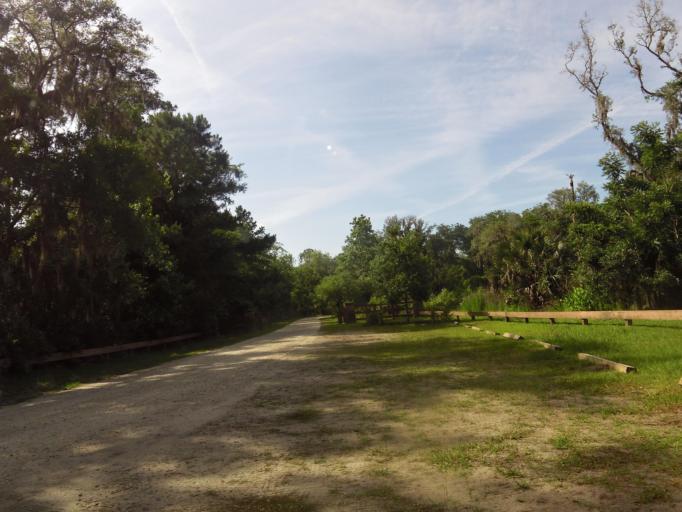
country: US
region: Florida
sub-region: Duval County
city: Atlantic Beach
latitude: 30.4866
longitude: -81.4907
